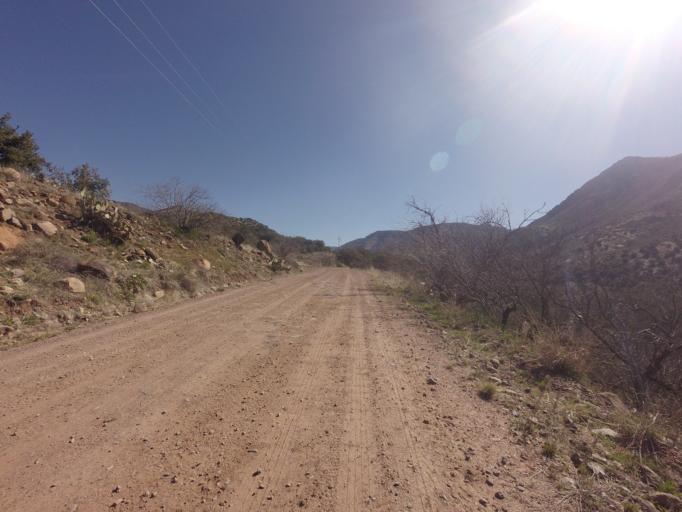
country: US
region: Arizona
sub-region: Gila County
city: Pine
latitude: 34.3936
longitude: -111.6484
